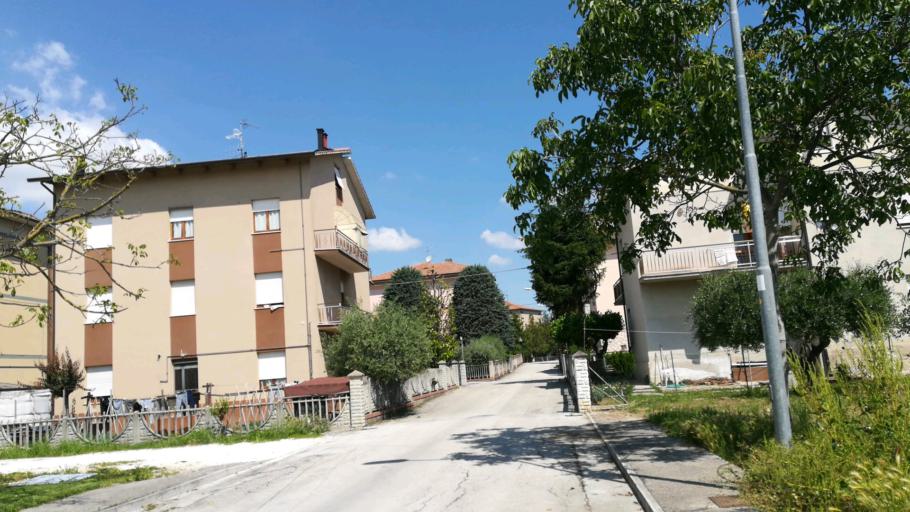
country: IT
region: The Marches
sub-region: Provincia di Macerata
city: Borgo Stazione
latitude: 43.2824
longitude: 13.6405
